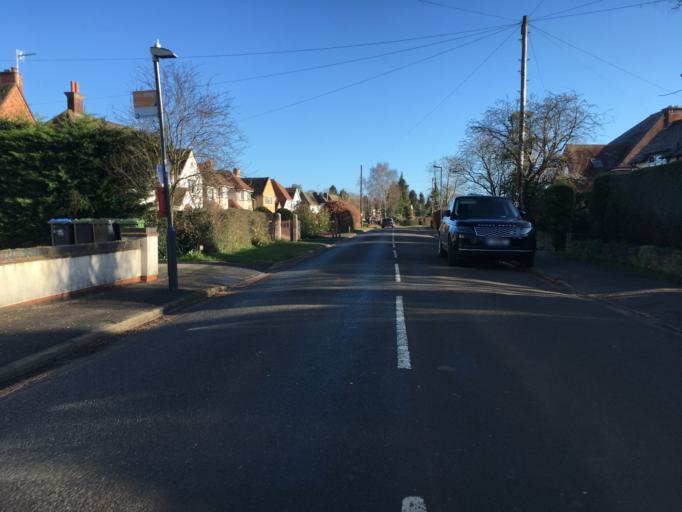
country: GB
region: England
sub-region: Warwickshire
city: Stratford-upon-Avon
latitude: 52.1901
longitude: -1.6815
